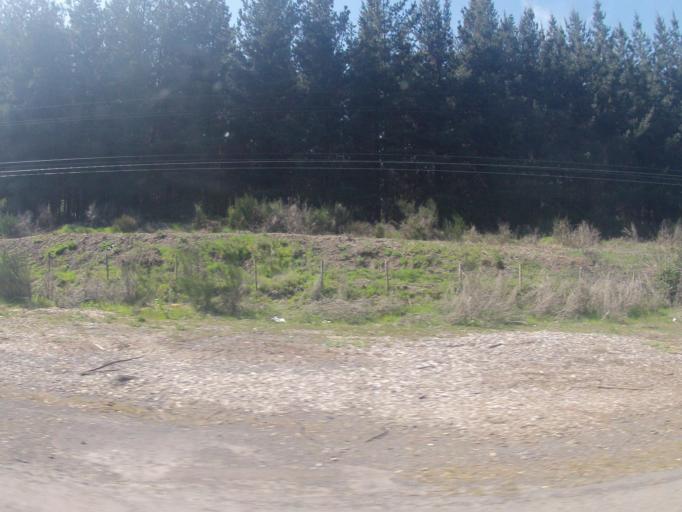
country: CL
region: Biobio
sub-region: Provincia de Biobio
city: Los Angeles
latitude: -37.3571
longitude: -72.3706
